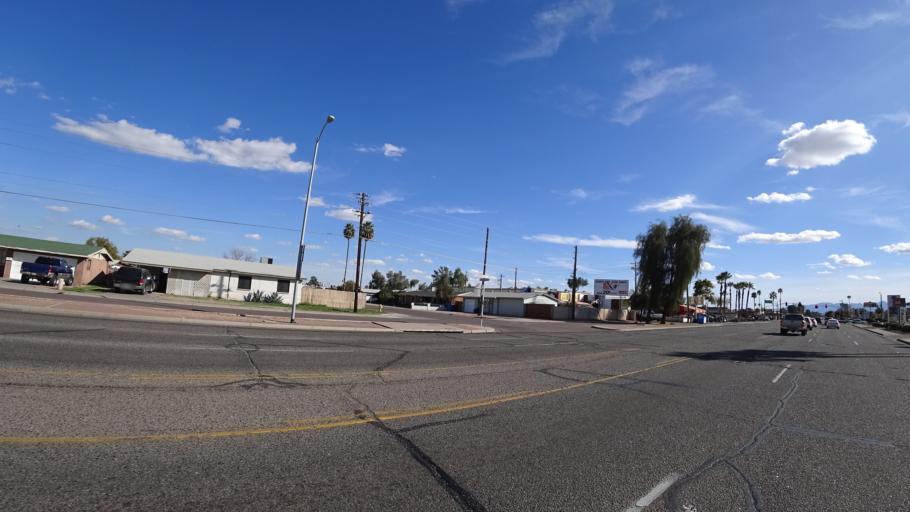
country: US
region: Arizona
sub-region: Maricopa County
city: Glendale
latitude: 33.4962
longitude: -112.2206
